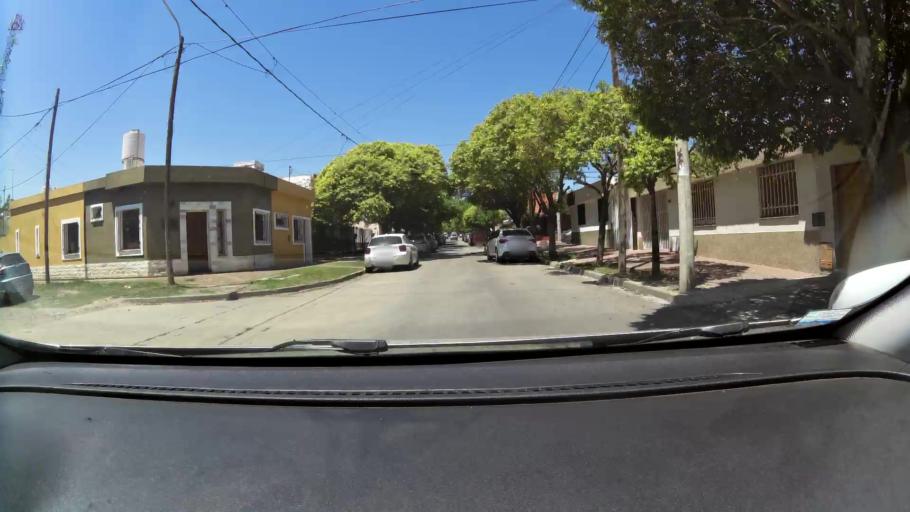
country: AR
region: Cordoba
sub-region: Departamento de Capital
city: Cordoba
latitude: -31.4114
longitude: -64.2170
